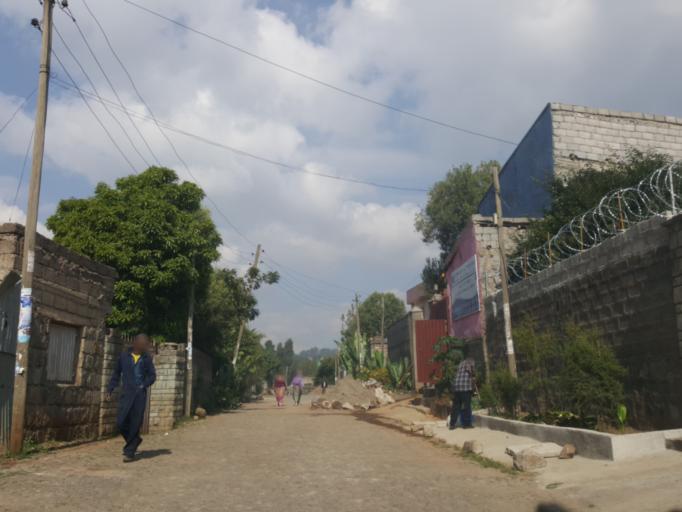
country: ET
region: Adis Abeba
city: Addis Ababa
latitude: 9.0550
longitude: 38.7186
